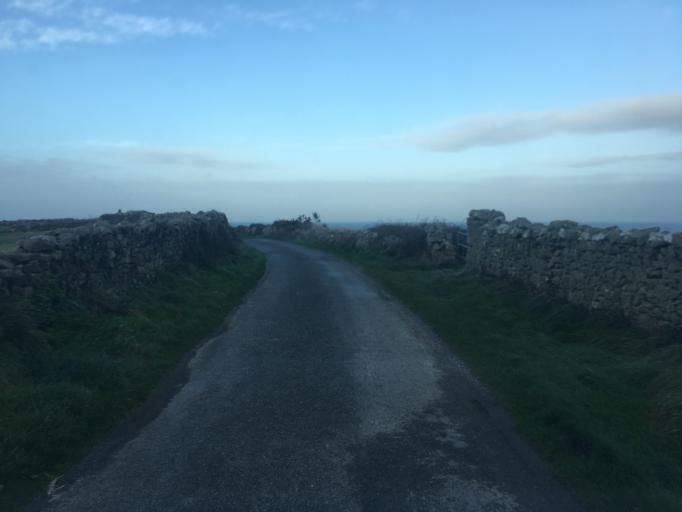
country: FR
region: Lower Normandy
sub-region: Departement de la Manche
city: Beaumont-Hague
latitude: 49.7244
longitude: -1.9235
